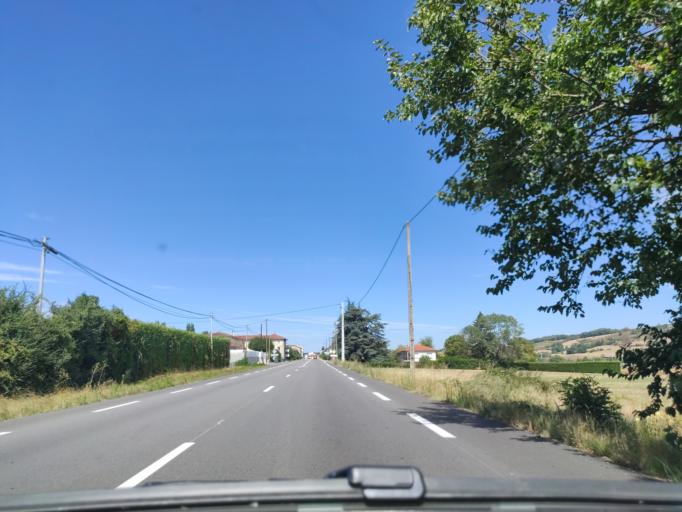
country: FR
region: Rhone-Alpes
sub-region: Departement de l'Isere
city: Reventin-Vaugris
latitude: 45.4679
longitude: 4.8278
